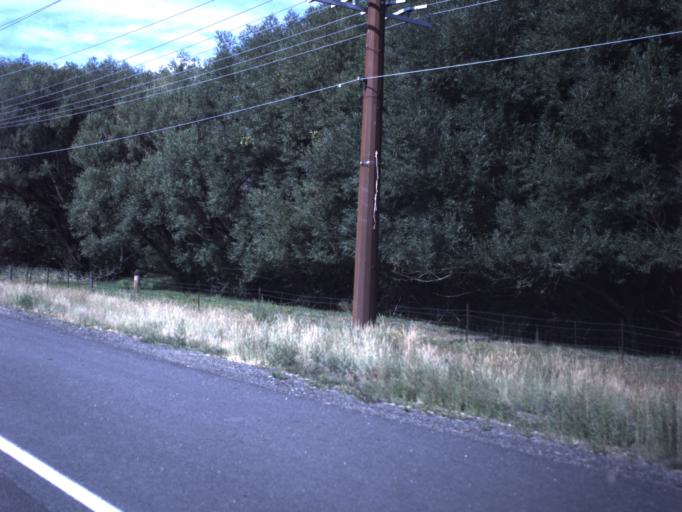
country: US
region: Utah
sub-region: Wasatch County
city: Heber
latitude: 40.5334
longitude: -111.4094
